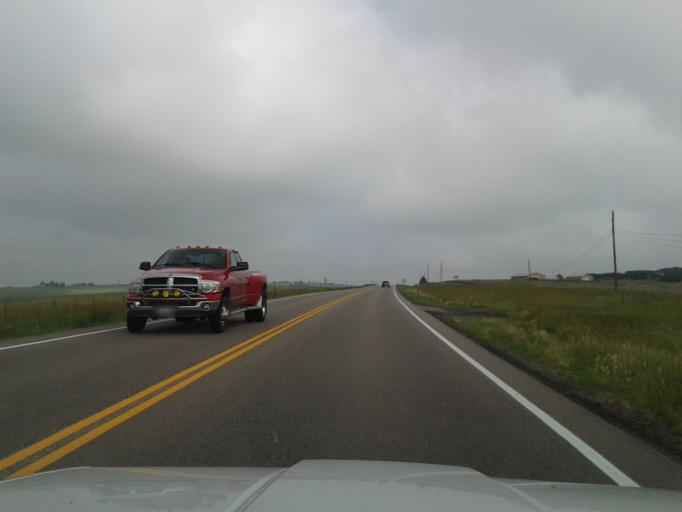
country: US
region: Colorado
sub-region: Elbert County
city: Ponderosa Park
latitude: 39.2681
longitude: -104.7298
